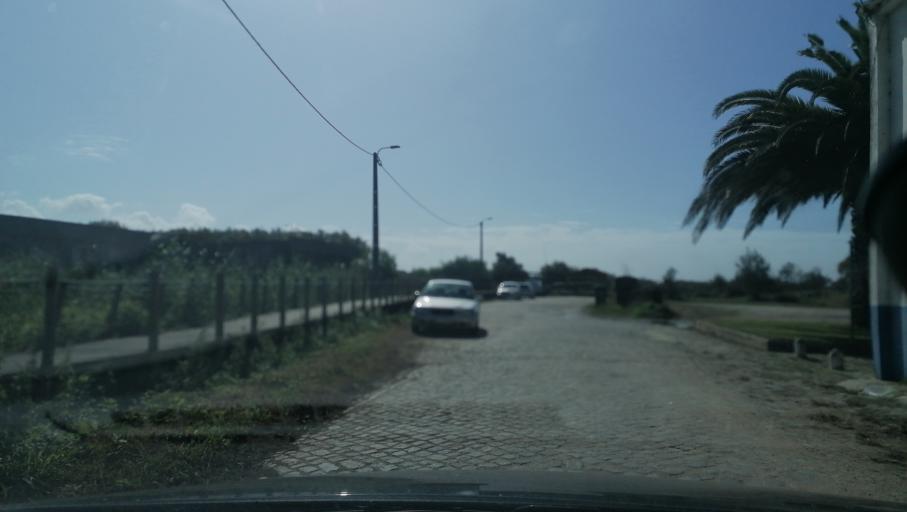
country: PT
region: Aveiro
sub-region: Ovar
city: Esmoriz
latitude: 40.9734
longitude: -8.6413
